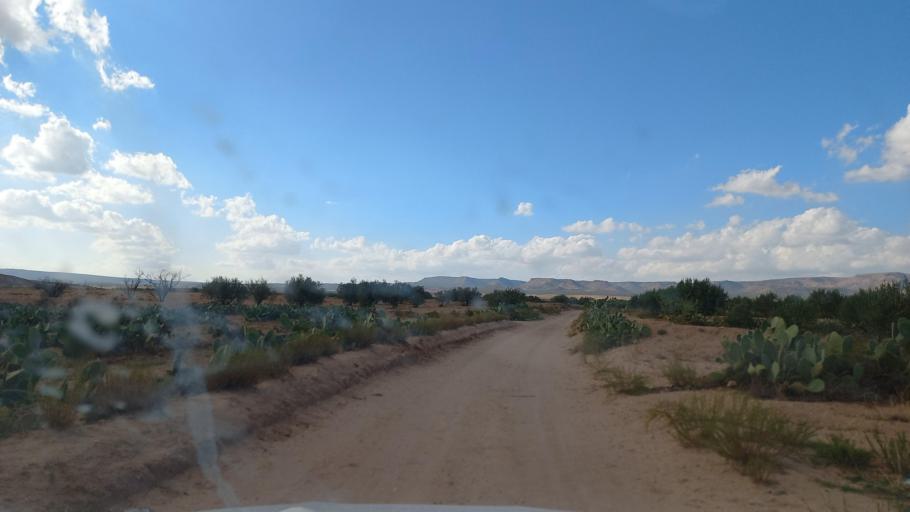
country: TN
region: Al Qasrayn
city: Sbiba
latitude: 35.3886
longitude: 9.0408
